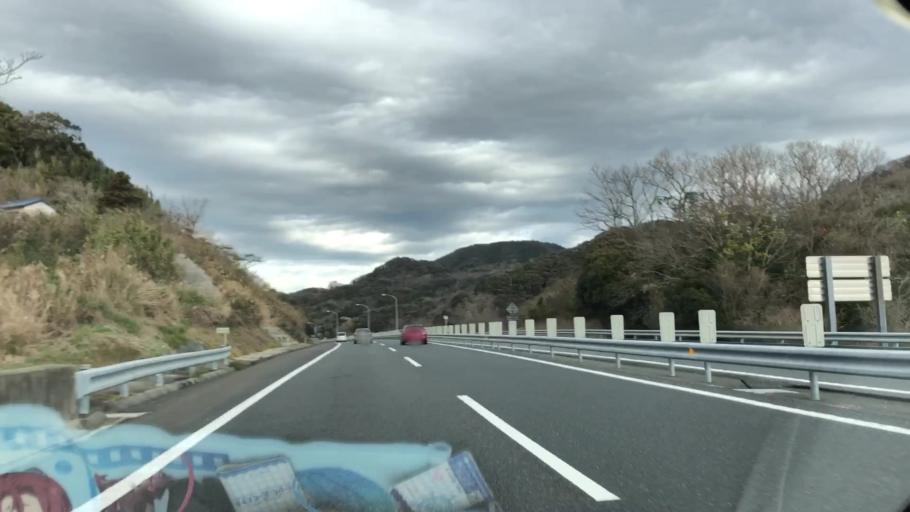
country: JP
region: Chiba
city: Tateyama
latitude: 35.0953
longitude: 139.8601
